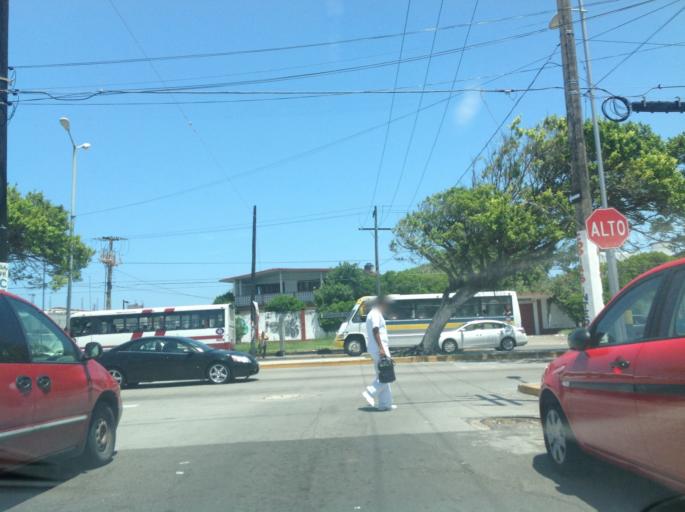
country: MX
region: Veracruz
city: Veracruz
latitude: 19.1590
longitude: -96.1315
